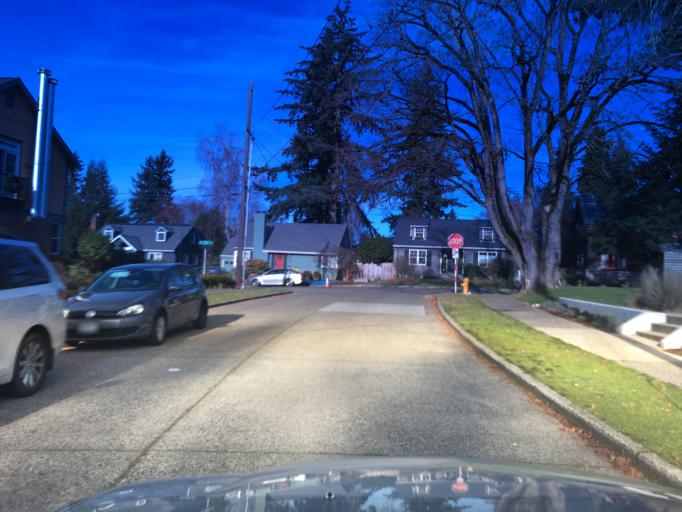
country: US
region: Washington
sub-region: King County
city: Inglewood-Finn Hill
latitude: 47.6791
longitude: -122.2759
